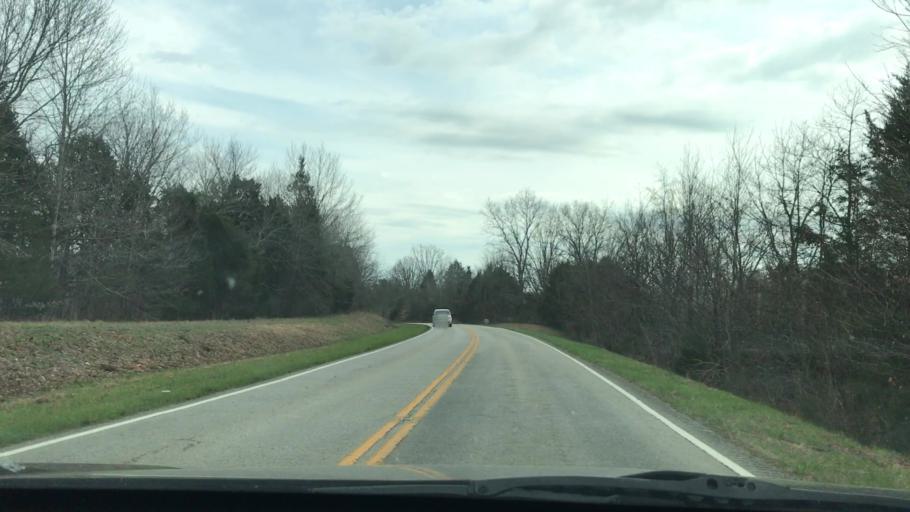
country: US
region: Kentucky
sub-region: Hart County
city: Munfordville
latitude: 37.3030
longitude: -85.7646
